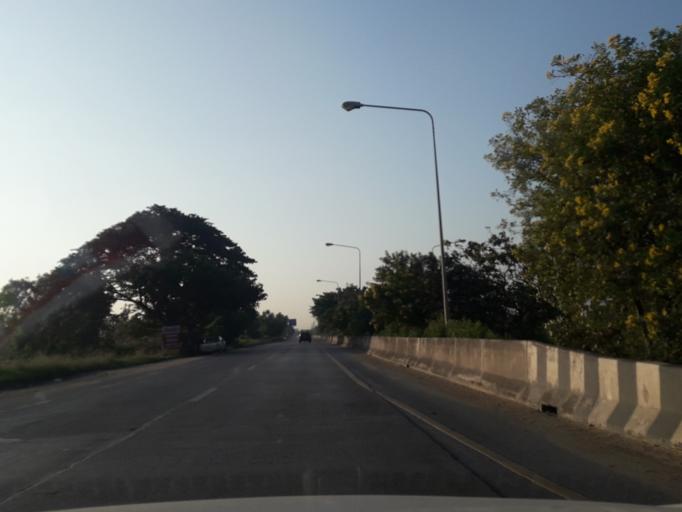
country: TH
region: Phra Nakhon Si Ayutthaya
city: Bang Pa-in
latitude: 14.1756
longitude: 100.5602
